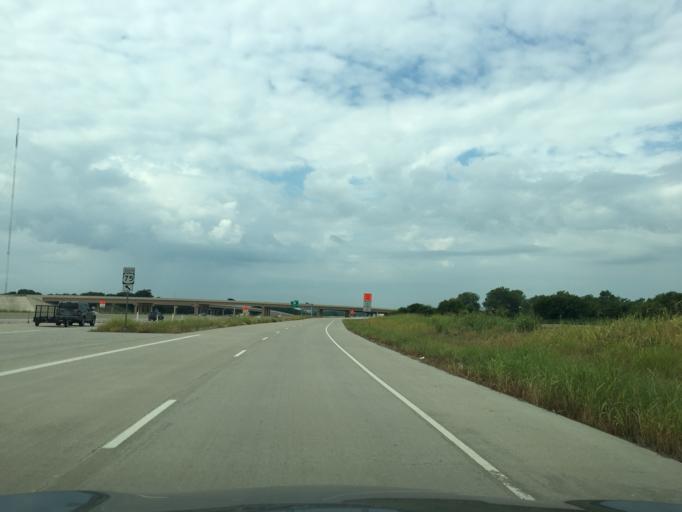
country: US
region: Texas
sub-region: Collin County
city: Melissa
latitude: 33.2676
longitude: -96.5971
